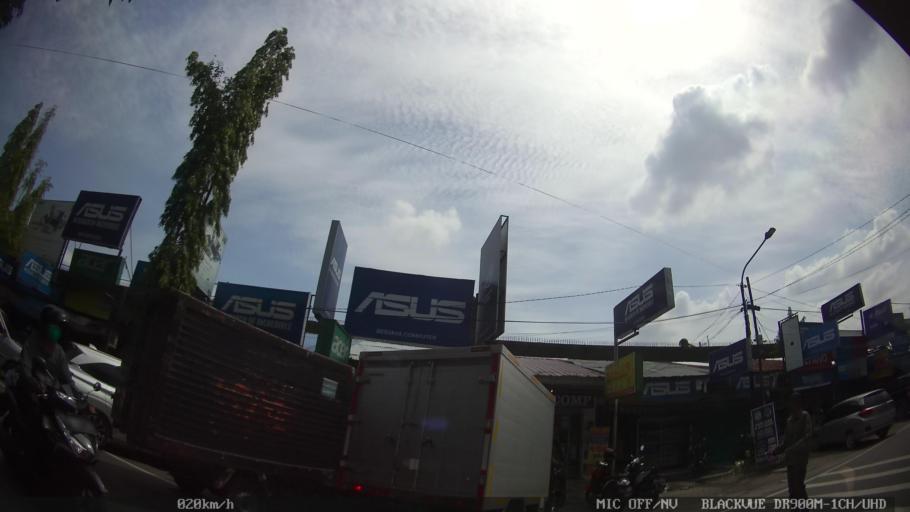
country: ID
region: North Sumatra
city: Medan
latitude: 3.5998
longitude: 98.6746
